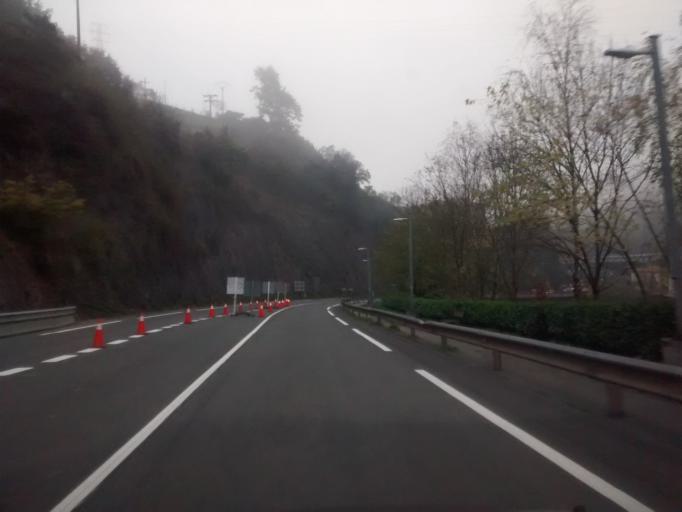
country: ES
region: Basque Country
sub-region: Provincia de Guipuzcoa
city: Eibar
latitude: 43.1907
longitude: -2.4551
